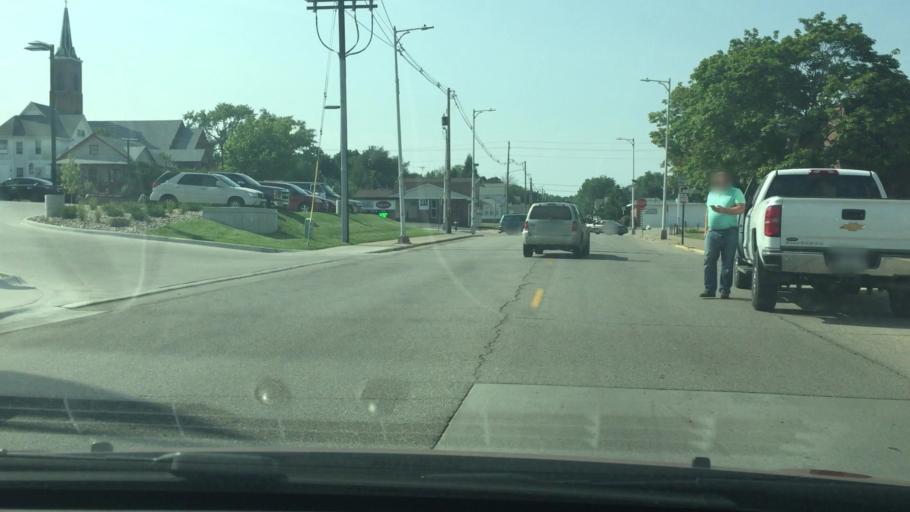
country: US
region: Iowa
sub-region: Muscatine County
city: Muscatine
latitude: 41.4243
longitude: -91.0453
